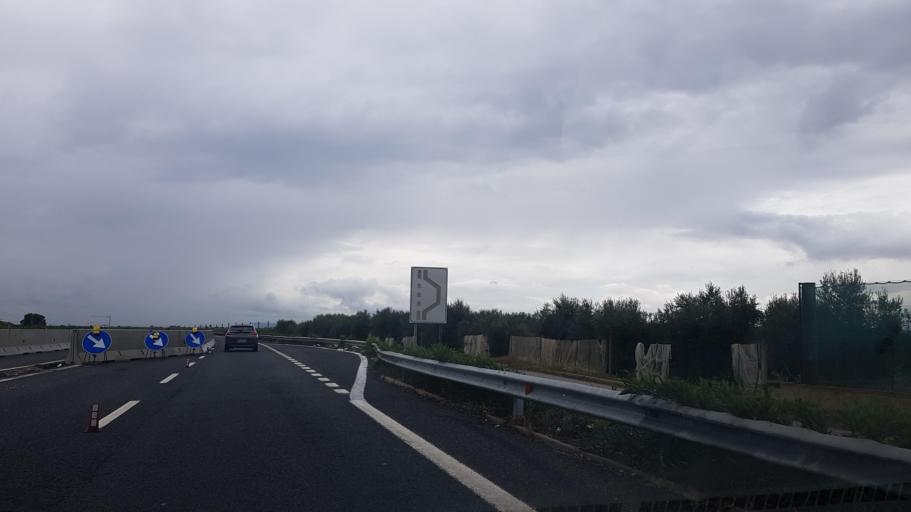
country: IT
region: Apulia
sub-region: Provincia di Taranto
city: Massafra
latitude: 40.5308
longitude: 17.1128
